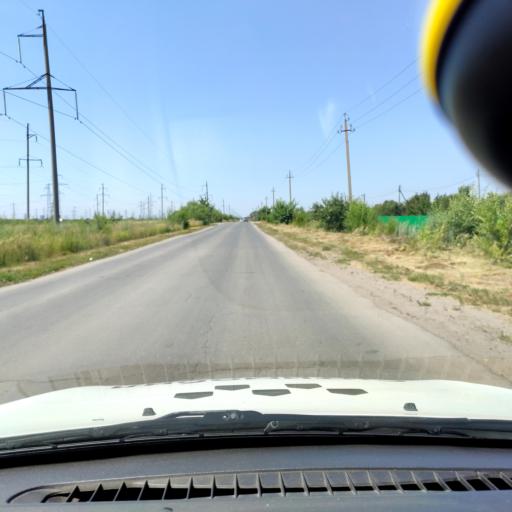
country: RU
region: Samara
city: Tol'yatti
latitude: 53.5899
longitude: 49.3212
